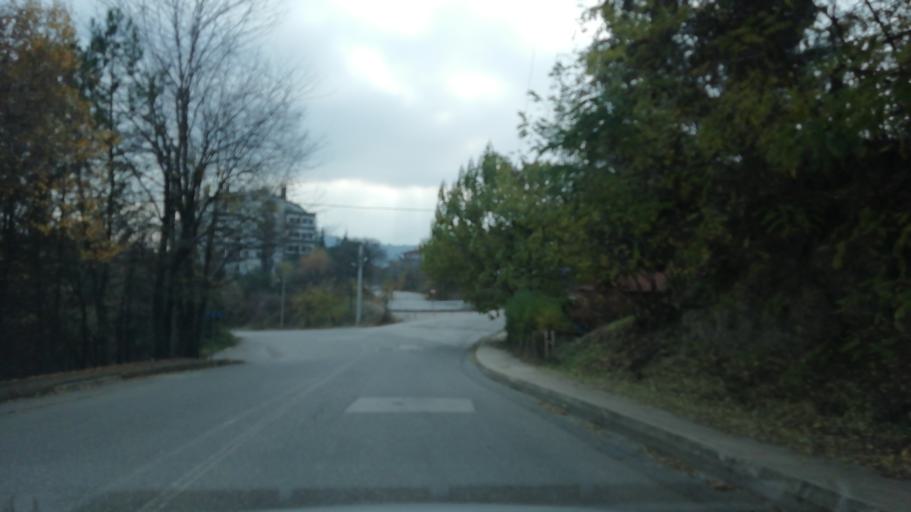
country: TR
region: Karabuk
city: Karabuk
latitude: 41.2002
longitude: 32.6232
